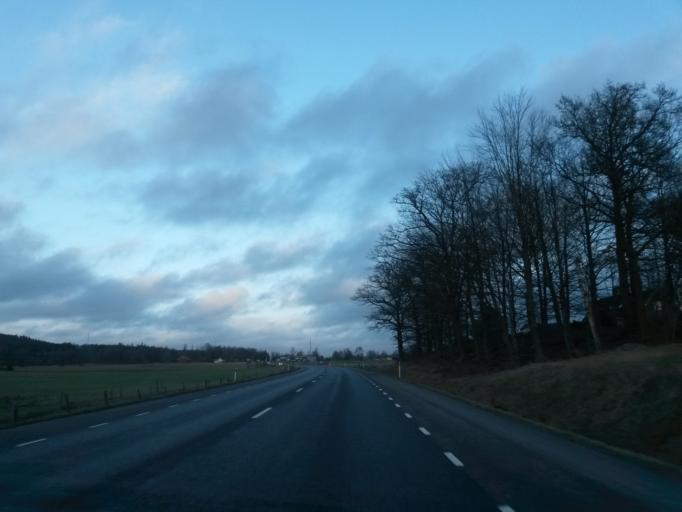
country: SE
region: Halland
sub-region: Halmstads Kommun
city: Aled
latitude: 56.7411
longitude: 12.9248
